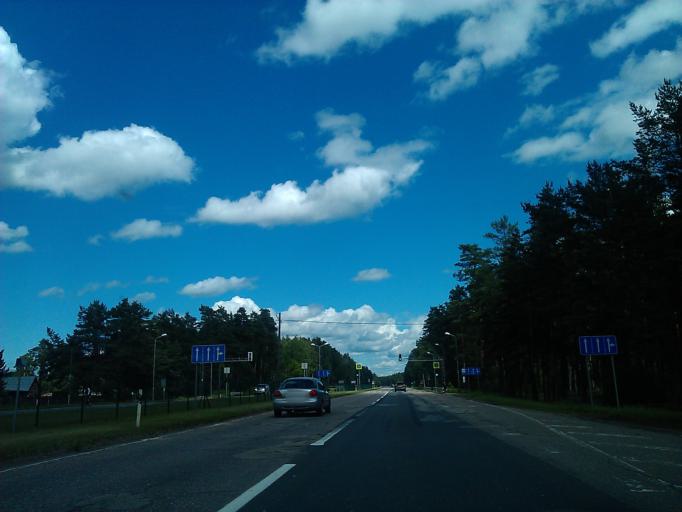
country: LV
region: Garkalne
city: Garkalne
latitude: 57.0415
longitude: 24.4216
